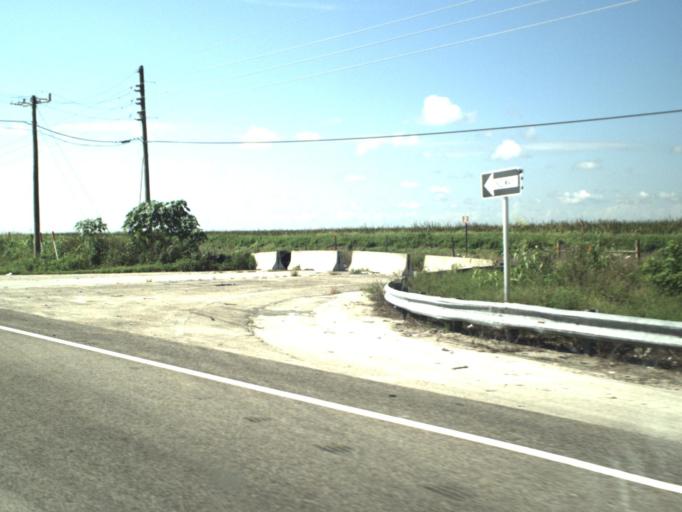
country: US
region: Florida
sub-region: Palm Beach County
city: Belle Glade Camp
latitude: 26.3853
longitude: -80.5770
